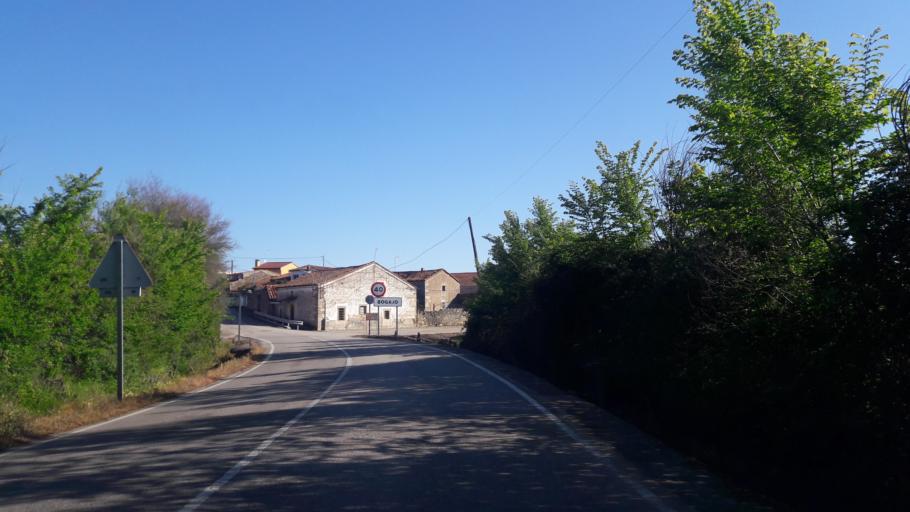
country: ES
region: Castille and Leon
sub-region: Provincia de Salamanca
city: Bogajo
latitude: 40.9038
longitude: -6.5306
